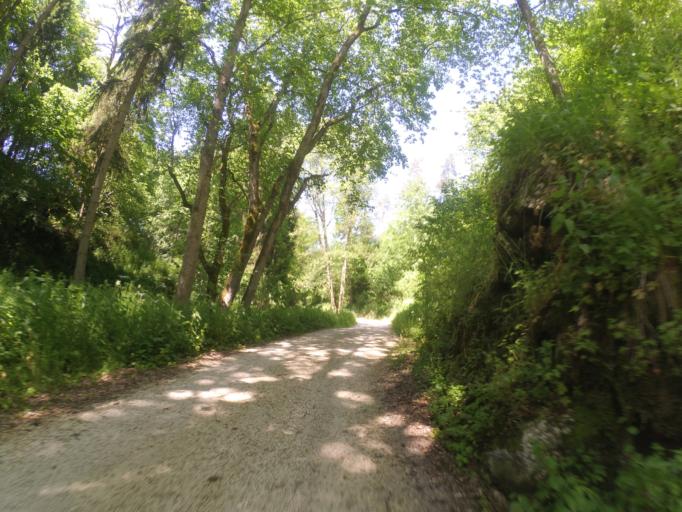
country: DE
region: Baden-Wuerttemberg
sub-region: Tuebingen Region
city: Berghulen
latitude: 48.4806
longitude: 9.8056
